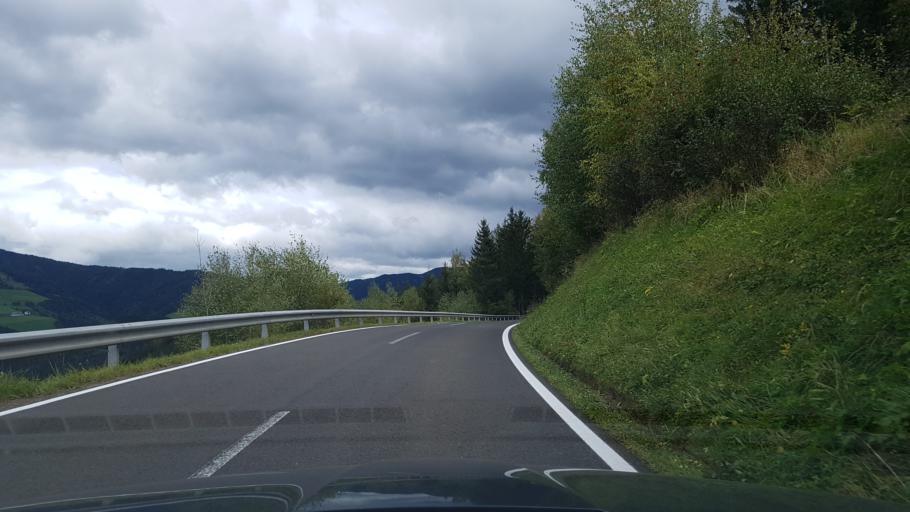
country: AT
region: Styria
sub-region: Politischer Bezirk Murtal
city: Kleinlobming
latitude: 47.1409
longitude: 14.8359
